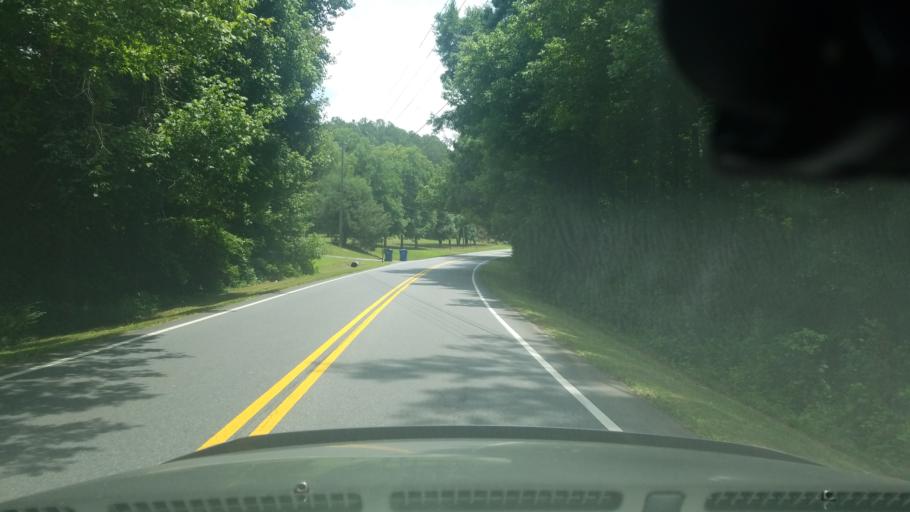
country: US
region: Georgia
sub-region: Fulton County
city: Milton
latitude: 34.1595
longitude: -84.2669
